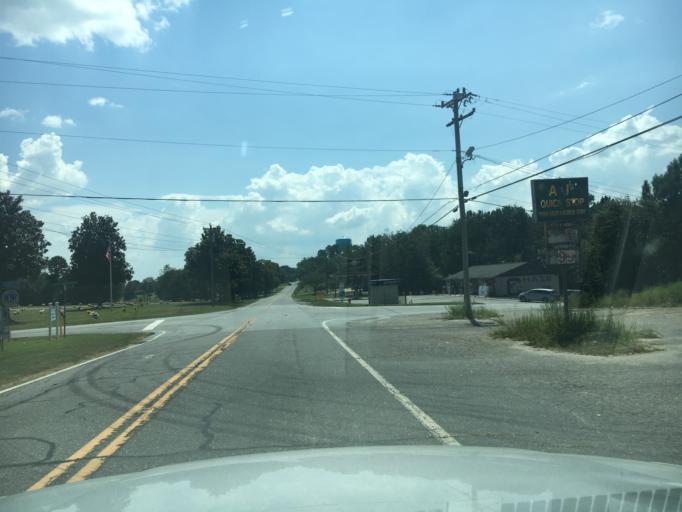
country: US
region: North Carolina
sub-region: Rutherford County
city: Forest City
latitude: 35.2475
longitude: -81.8453
